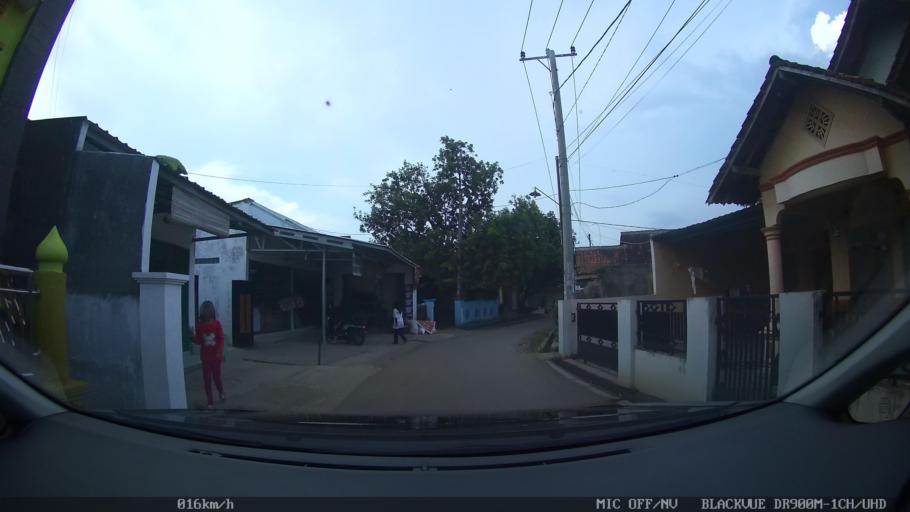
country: ID
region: Lampung
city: Kedaton
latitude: -5.3919
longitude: 105.2055
